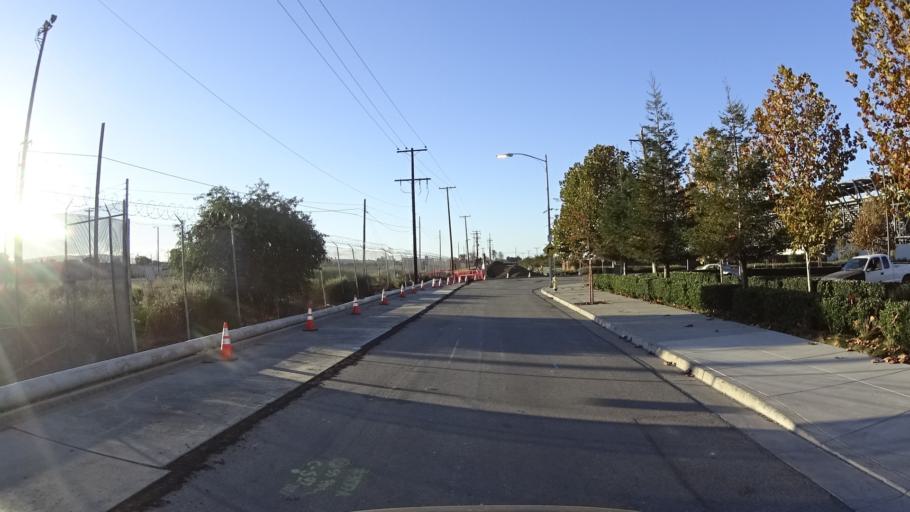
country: US
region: California
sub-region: Santa Clara County
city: Burbank
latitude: 37.3491
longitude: -121.9241
